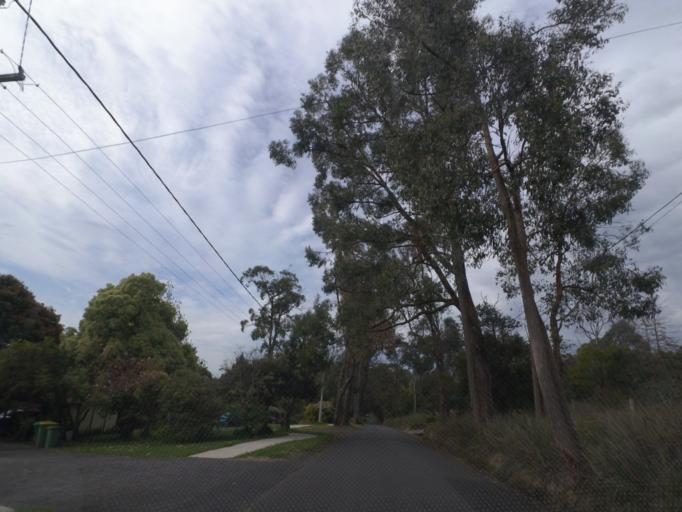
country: AU
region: Victoria
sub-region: Yarra Ranges
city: Montrose
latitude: -37.8102
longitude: 145.3582
